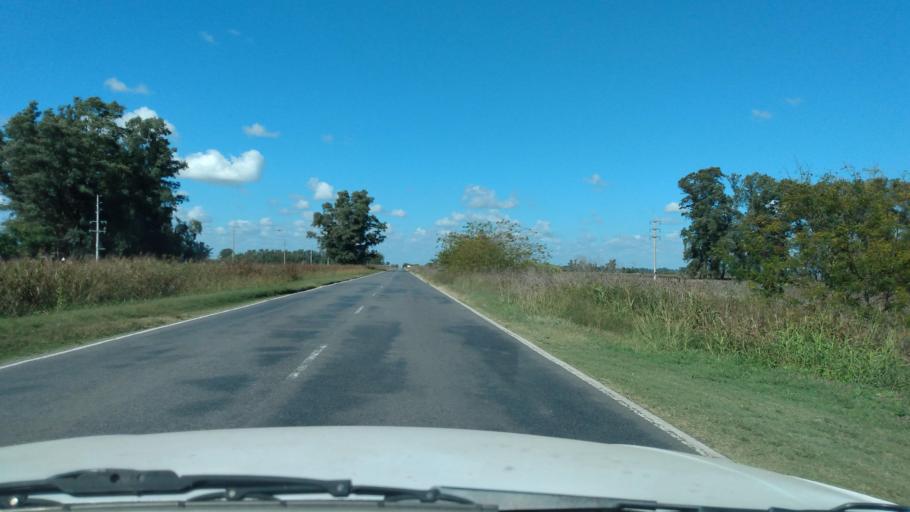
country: AR
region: Buenos Aires
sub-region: Partido de Mercedes
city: Mercedes
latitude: -34.7397
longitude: -59.3857
